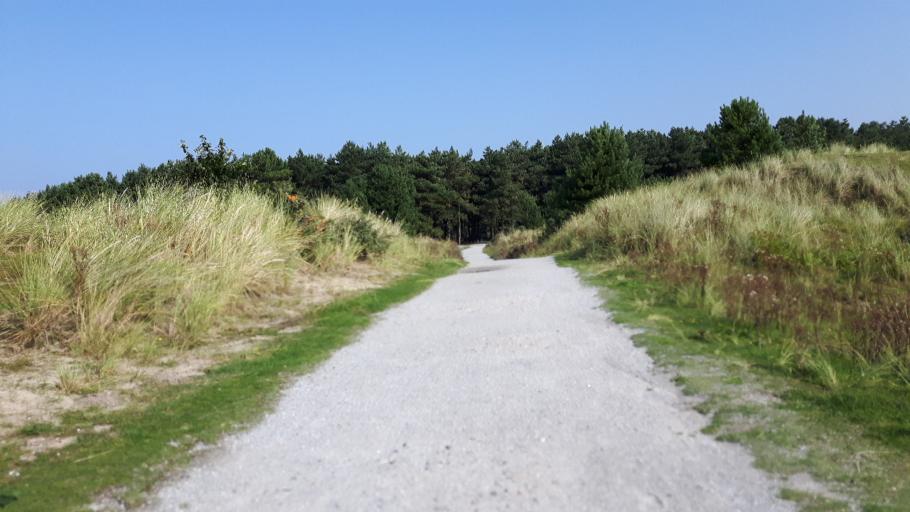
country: NL
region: Friesland
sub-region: Gemeente Ameland
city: Nes
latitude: 53.4582
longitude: 5.8148
